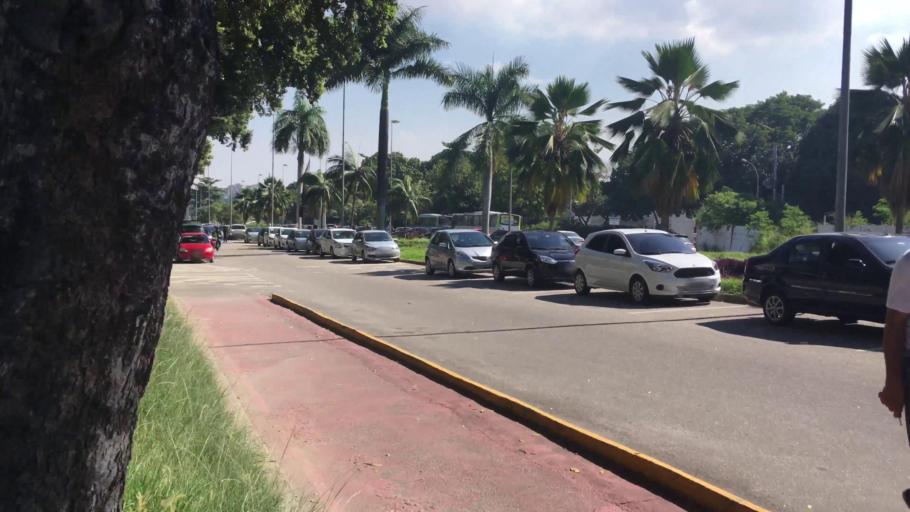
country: BR
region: Rio de Janeiro
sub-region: Rio De Janeiro
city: Rio de Janeiro
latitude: -22.8580
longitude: -43.2306
